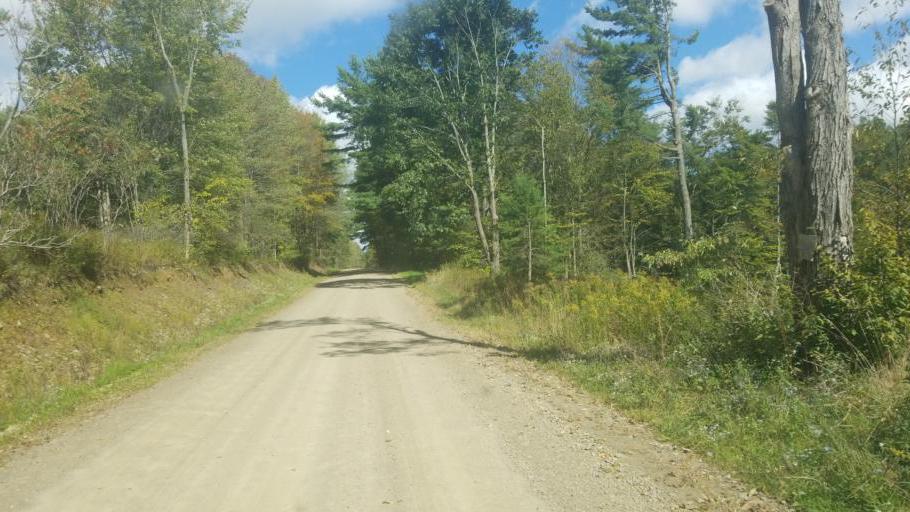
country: US
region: New York
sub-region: Allegany County
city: Cuba
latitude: 42.1759
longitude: -78.3317
